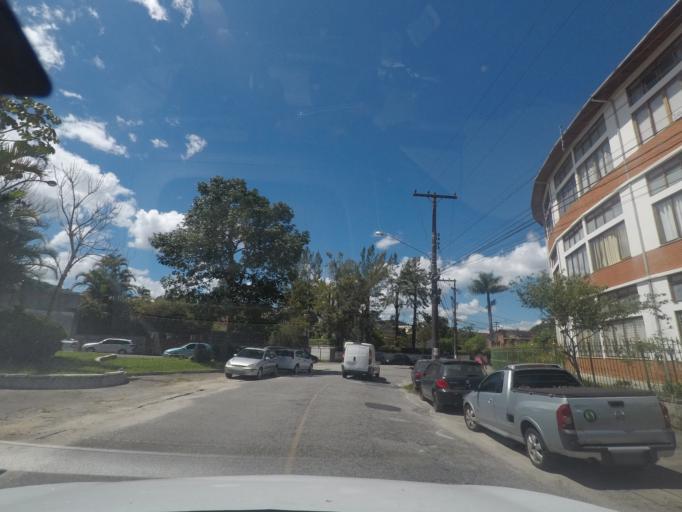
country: BR
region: Rio de Janeiro
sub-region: Teresopolis
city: Teresopolis
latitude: -22.4317
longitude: -42.9783
